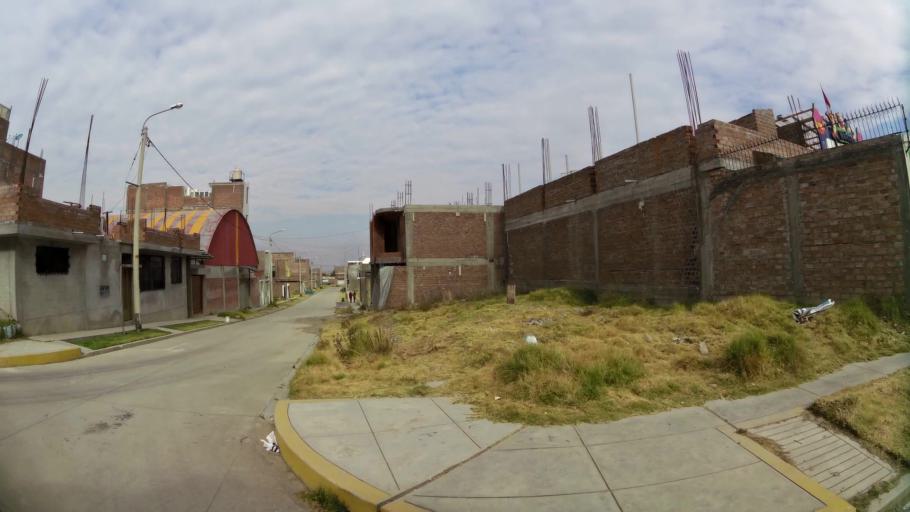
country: PE
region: Junin
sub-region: Provincia de Huancayo
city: Huancayo
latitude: -12.0495
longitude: -75.1868
